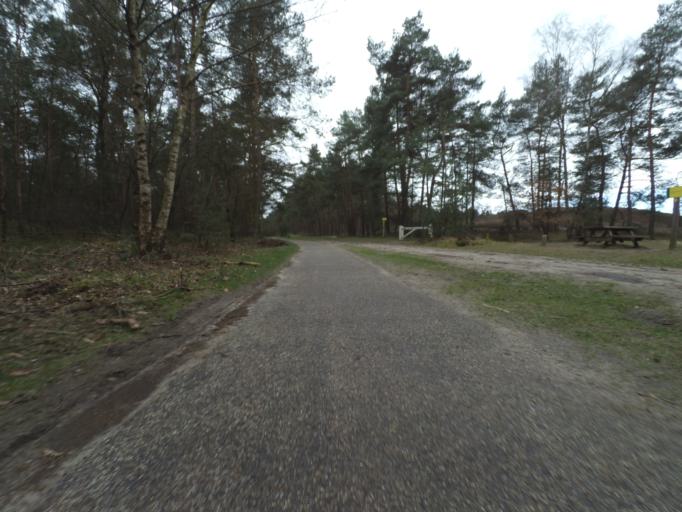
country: NL
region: Gelderland
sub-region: Gemeente Apeldoorn
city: Loenen
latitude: 52.0937
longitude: 6.0208
